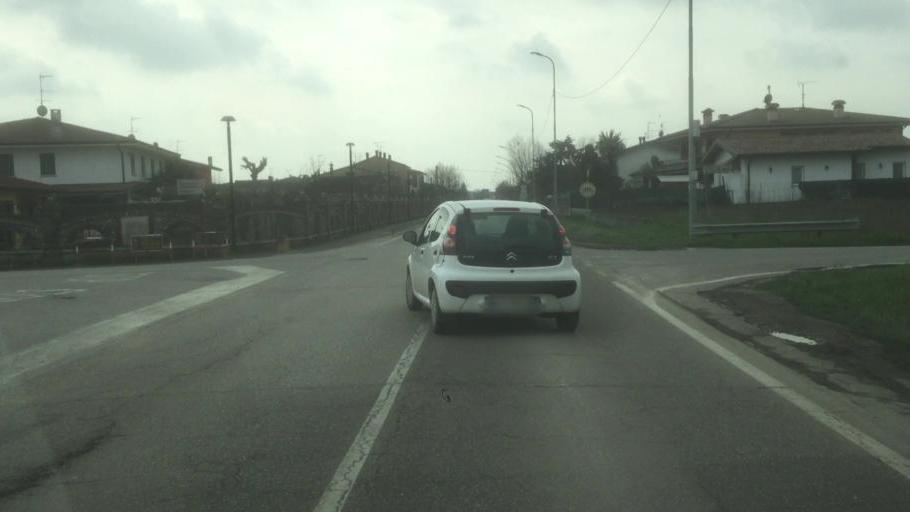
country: IT
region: Lombardy
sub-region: Provincia di Mantova
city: Casaloldo
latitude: 45.2592
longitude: 10.4761
